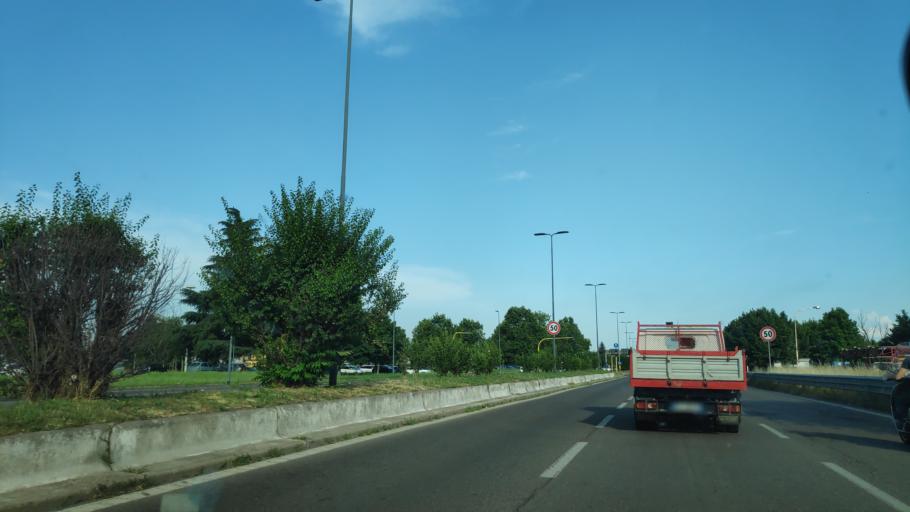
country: IT
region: Lombardy
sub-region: Citta metropolitana di Milano
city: Noverasco-Sporting Mirasole
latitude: 45.4214
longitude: 9.2010
